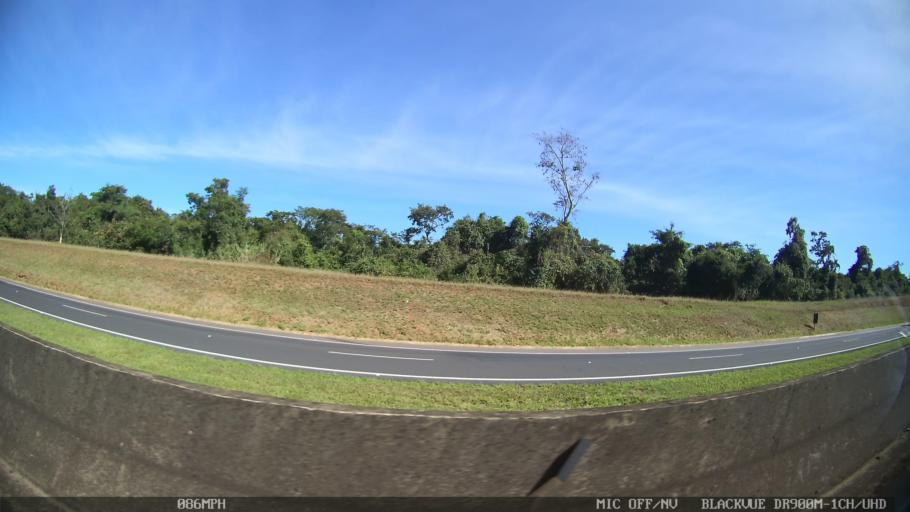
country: BR
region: Sao Paulo
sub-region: Pirassununga
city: Pirassununga
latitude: -21.9407
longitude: -47.4655
